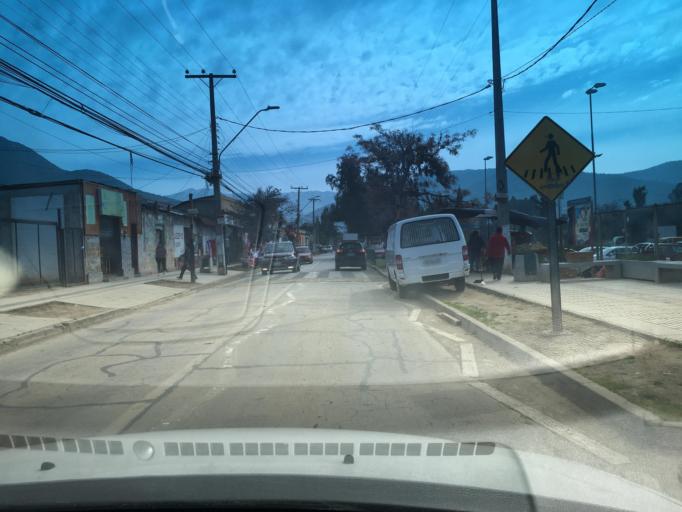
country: CL
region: Santiago Metropolitan
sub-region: Provincia de Chacabuco
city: Lampa
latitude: -33.0846
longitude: -70.9290
